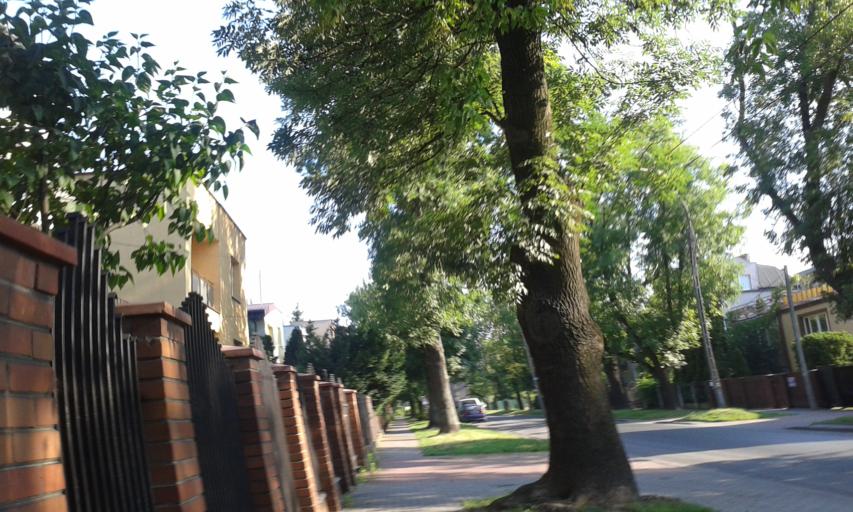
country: PL
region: Masovian Voivodeship
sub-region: Warszawa
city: Ursus
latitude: 52.1935
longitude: 20.8827
